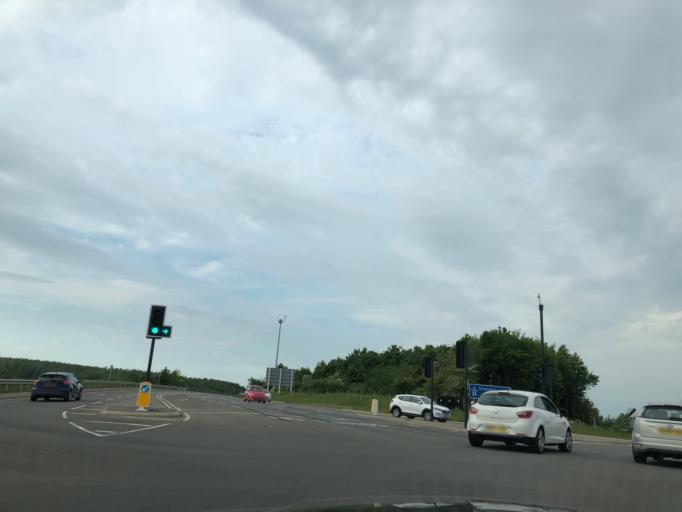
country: GB
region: England
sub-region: Warwickshire
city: Harbury
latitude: 52.1910
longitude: -1.4605
